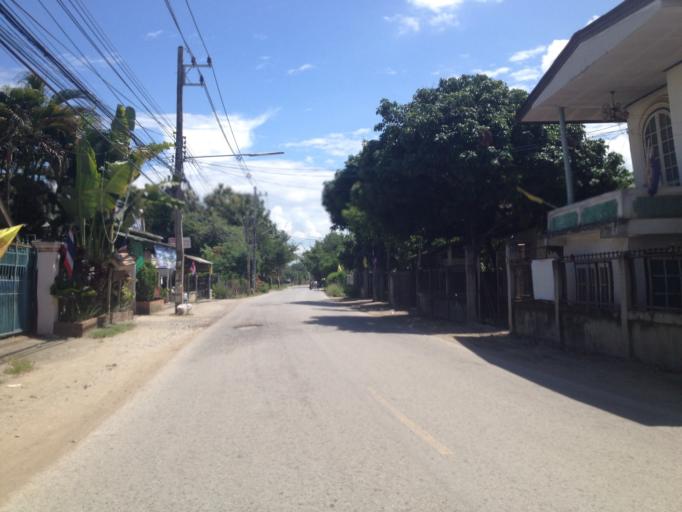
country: TH
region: Chiang Mai
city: San Pa Tong
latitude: 18.6398
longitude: 98.9296
